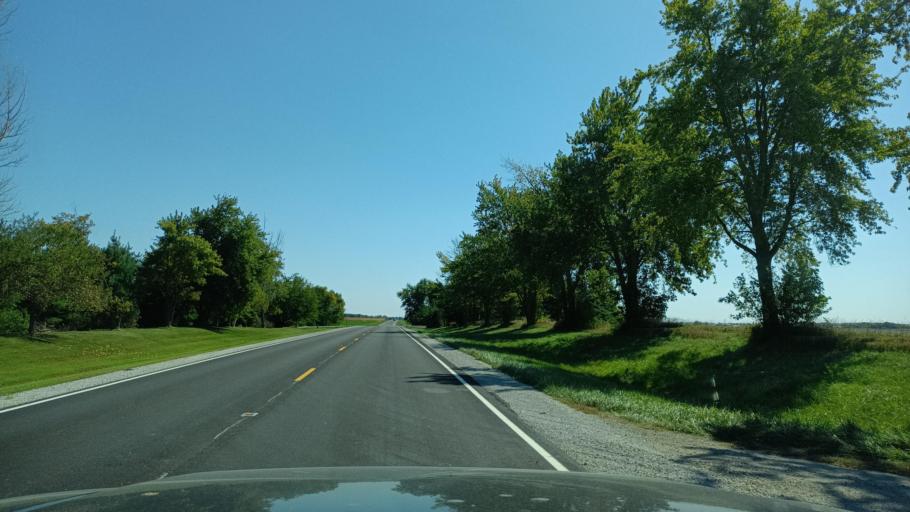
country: US
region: Illinois
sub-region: McLean County
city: Twin Grove
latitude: 40.5613
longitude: -89.0820
